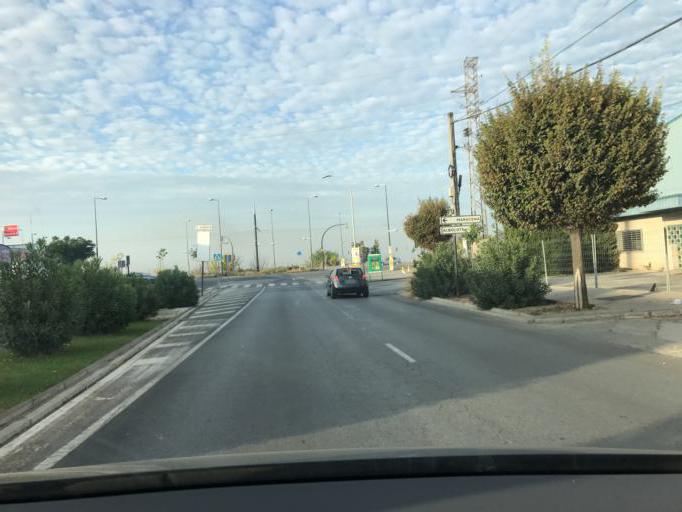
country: ES
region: Andalusia
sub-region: Provincia de Granada
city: Albolote
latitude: 37.2235
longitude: -3.6453
